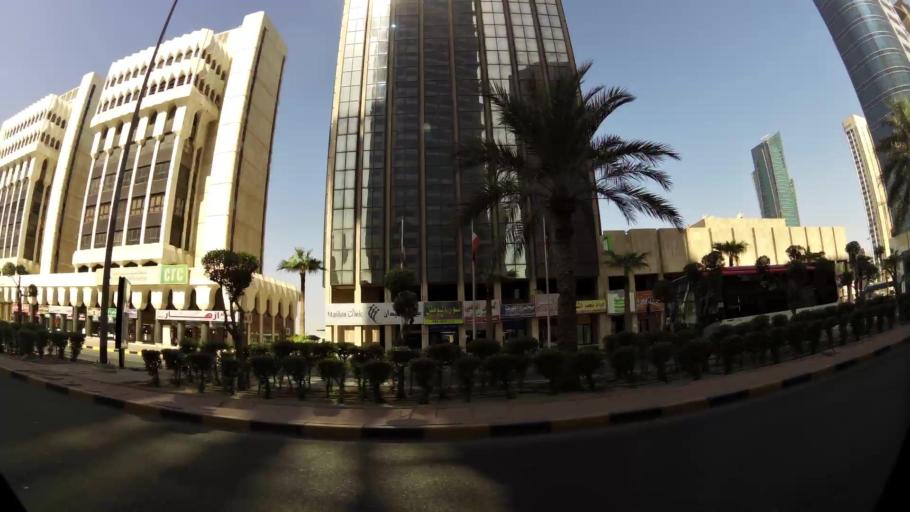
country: KW
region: Al Asimah
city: Kuwait City
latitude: 29.3817
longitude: 47.9857
